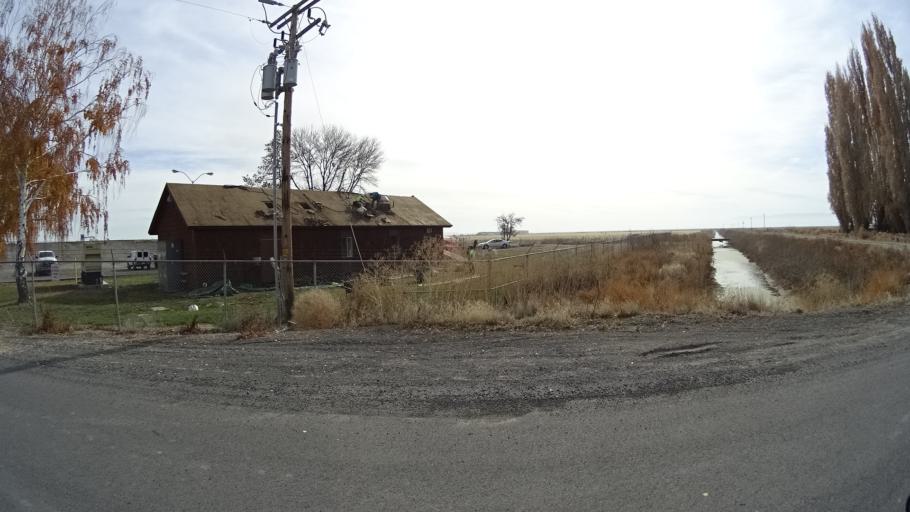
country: US
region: California
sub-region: Siskiyou County
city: Tulelake
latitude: 41.9482
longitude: -121.4717
